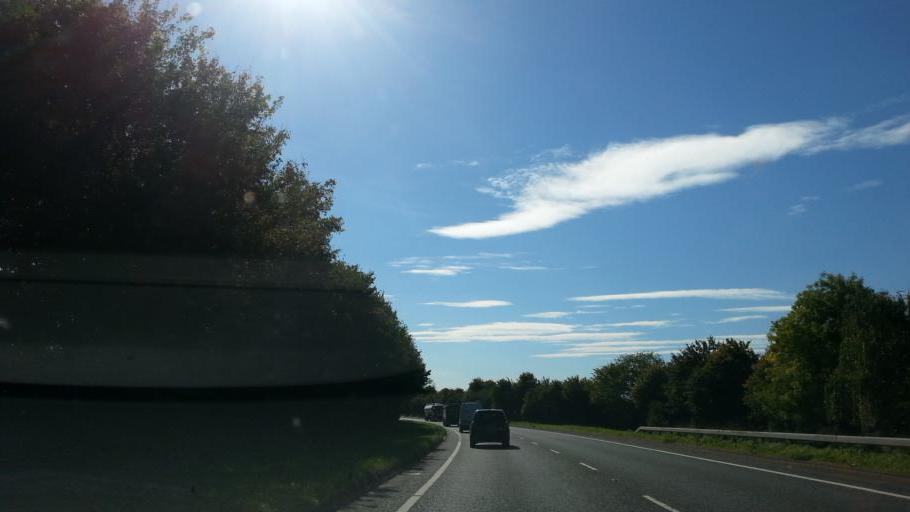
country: GB
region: England
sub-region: Telford and Wrekin
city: Chetwynd
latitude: 52.7494
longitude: -2.3952
